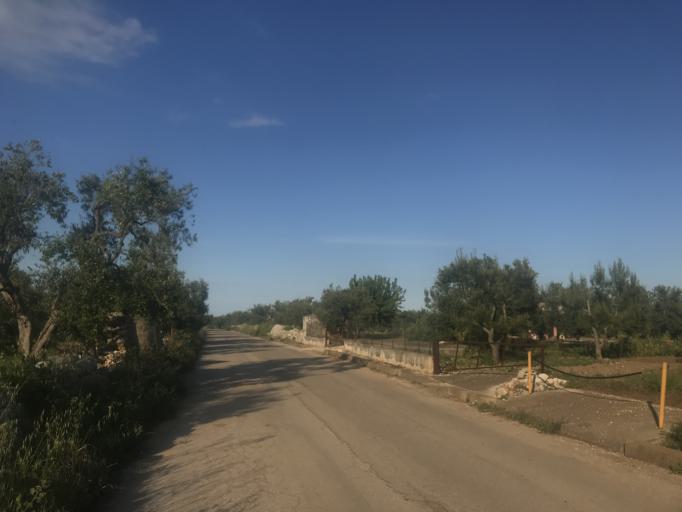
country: IT
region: Apulia
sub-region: Provincia di Bari
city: Corato
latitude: 41.1604
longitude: 16.4181
